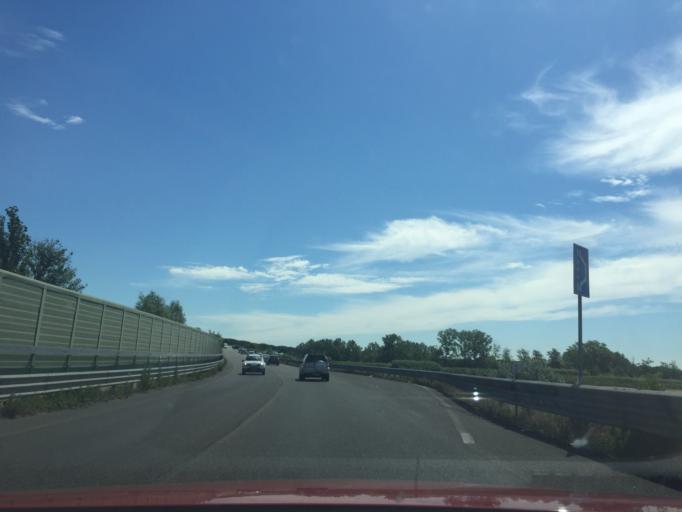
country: IT
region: Tuscany
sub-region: Province of Pisa
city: Pontedera
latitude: 43.6765
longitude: 10.6343
